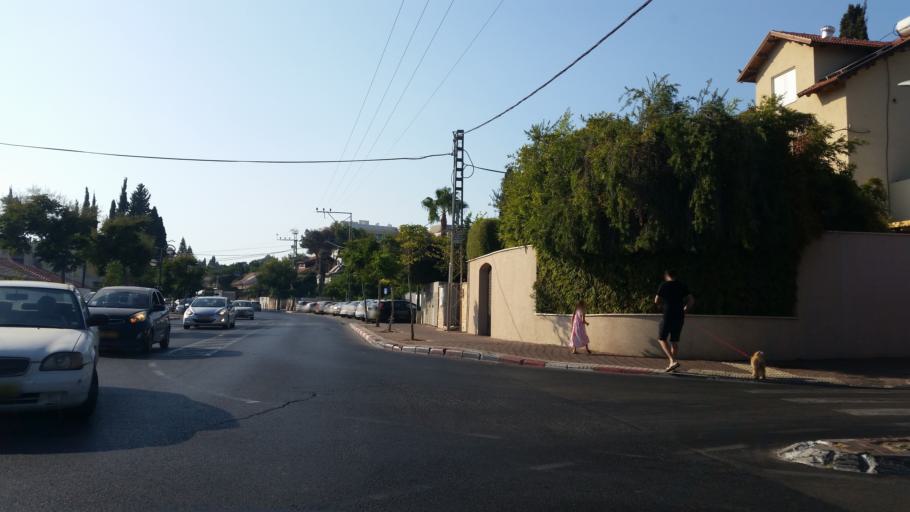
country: IL
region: Tel Aviv
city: Ramat HaSharon
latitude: 32.1350
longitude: 34.8519
